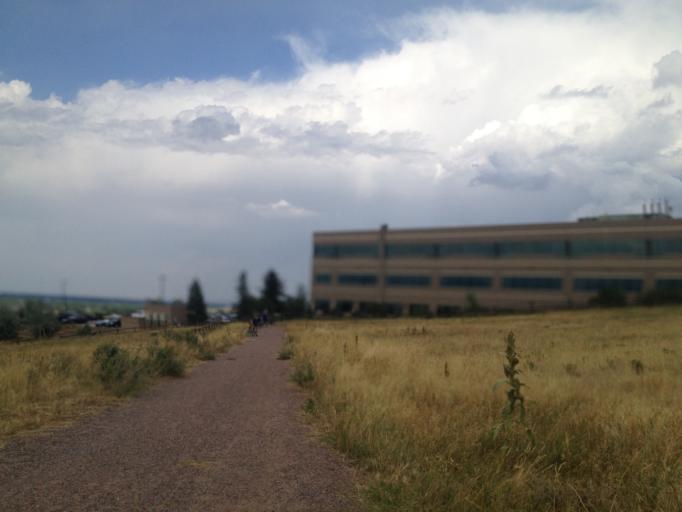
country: US
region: Colorado
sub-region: Boulder County
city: Superior
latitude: 39.9454
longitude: -105.1665
